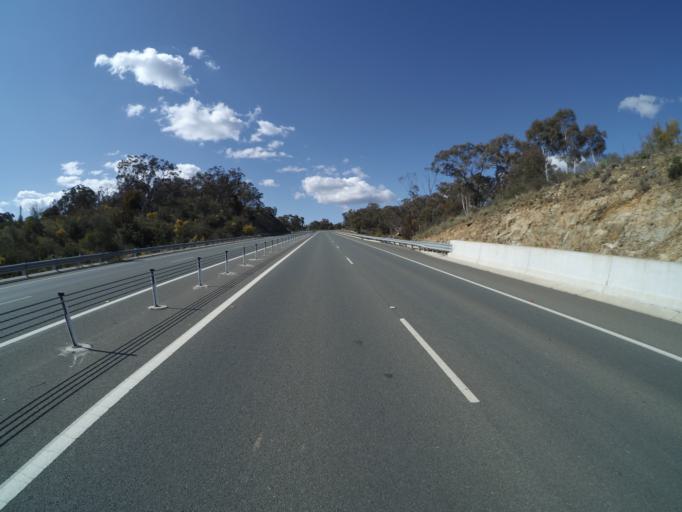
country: AU
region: New South Wales
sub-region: Queanbeyan
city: Queanbeyan
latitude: -35.3430
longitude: 149.2521
